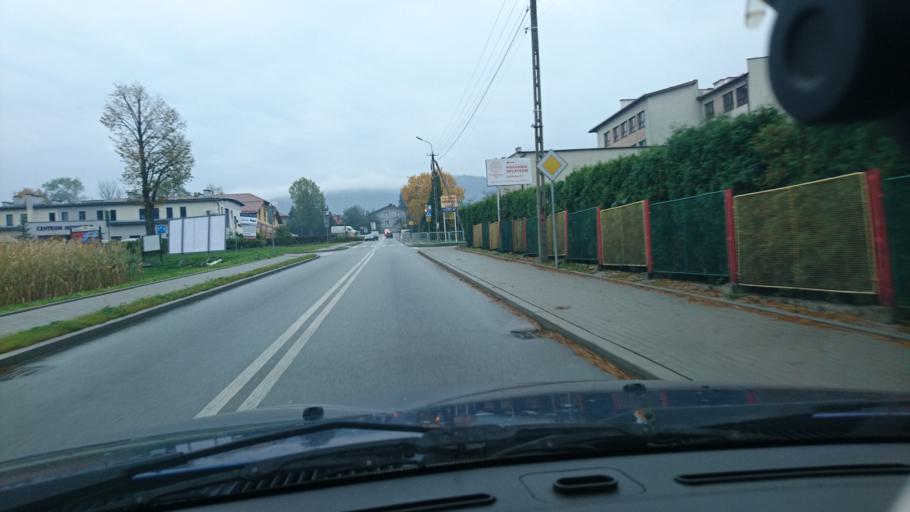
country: PL
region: Silesian Voivodeship
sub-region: Powiat bielski
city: Kozy
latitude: 49.8482
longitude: 19.1463
